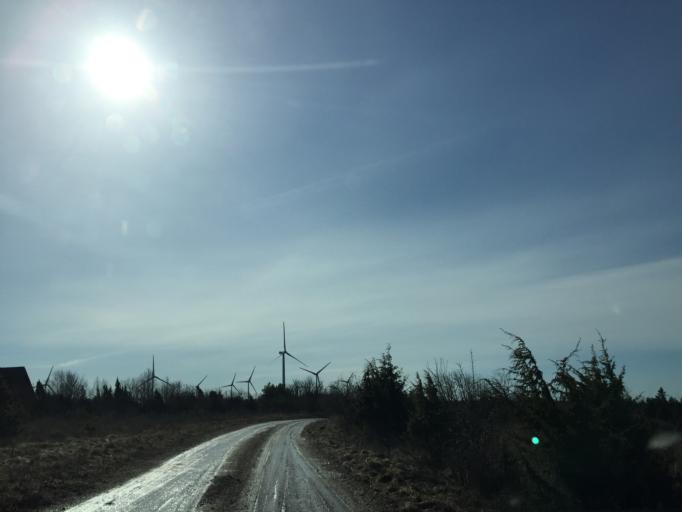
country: EE
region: Laeaene
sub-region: Haapsalu linn
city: Haapsalu
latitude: 58.6473
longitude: 23.5126
